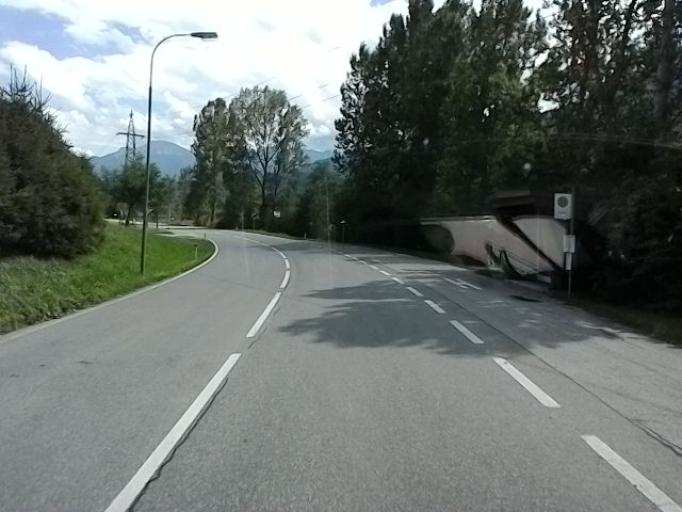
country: AT
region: Tyrol
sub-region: Politischer Bezirk Innsbruck Land
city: Inzing
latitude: 47.2844
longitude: 11.1900
